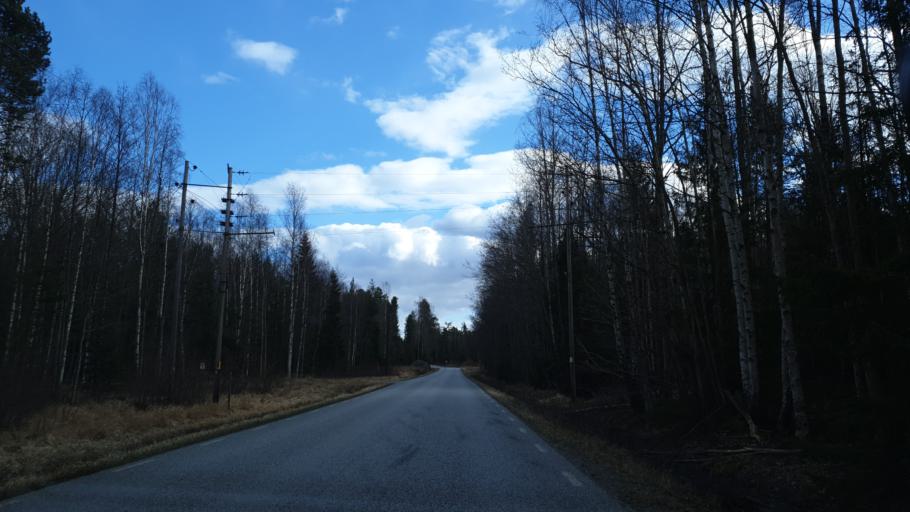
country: SE
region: Stockholm
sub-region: Varmdo Kommun
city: Hemmesta
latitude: 59.2338
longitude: 18.4812
